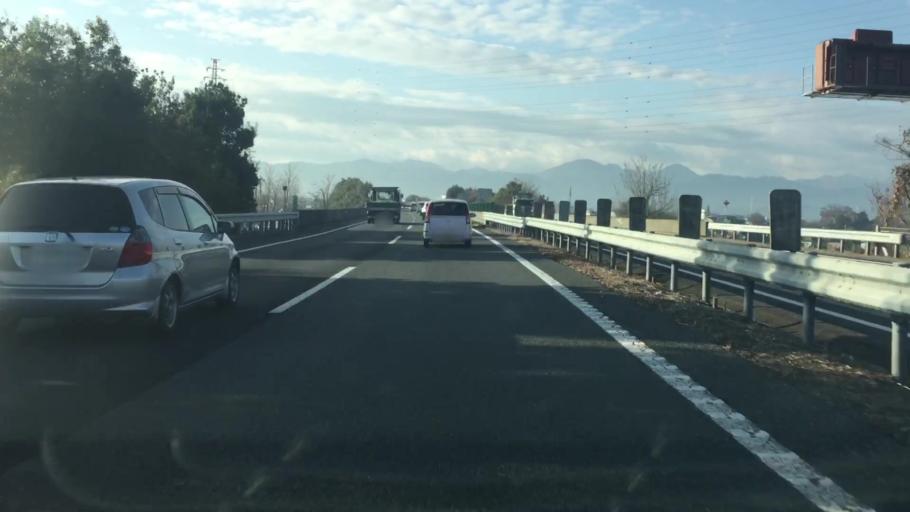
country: JP
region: Gunma
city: Fujioka
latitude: 36.2683
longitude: 139.0717
